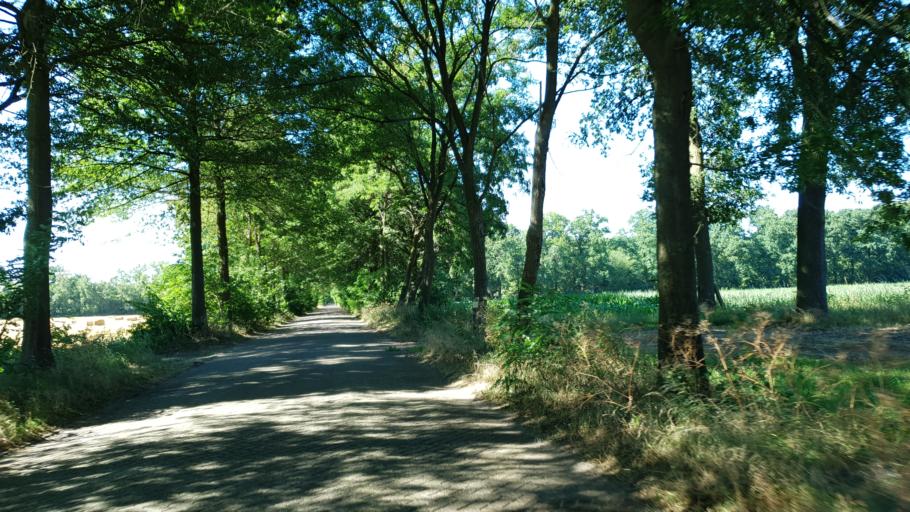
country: BE
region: Flanders
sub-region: Provincie Antwerpen
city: Merksplas
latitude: 51.3640
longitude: 4.8271
